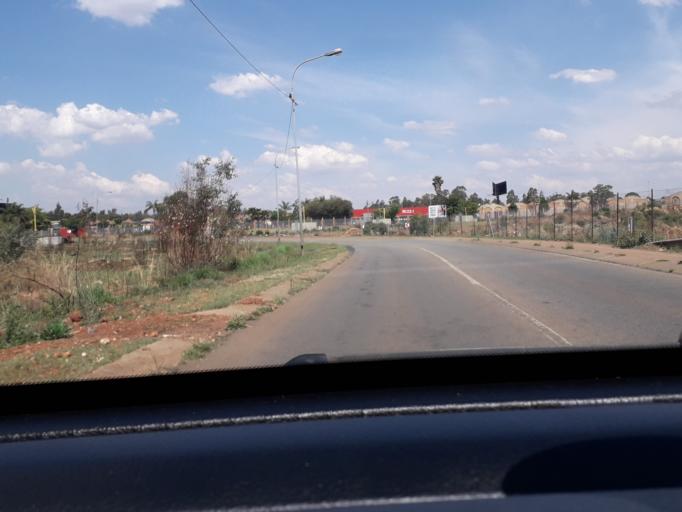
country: ZA
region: Gauteng
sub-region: City of Tshwane Metropolitan Municipality
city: Centurion
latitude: -25.8499
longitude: 28.2240
